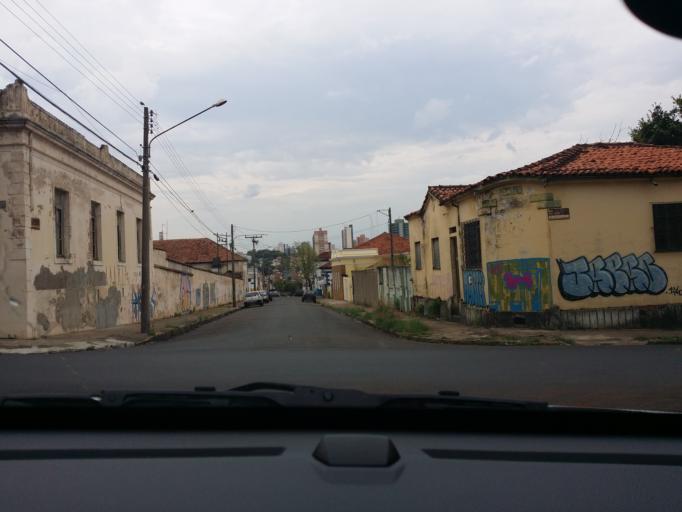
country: BR
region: Sao Paulo
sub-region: Sao Carlos
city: Sao Carlos
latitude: -22.0237
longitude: -47.8945
